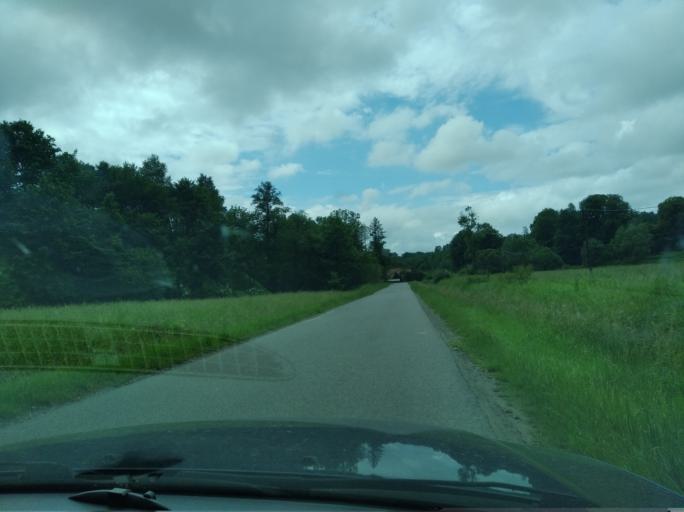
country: PL
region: Subcarpathian Voivodeship
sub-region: Powiat przemyski
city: Dubiecko
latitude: 49.8389
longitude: 22.4009
